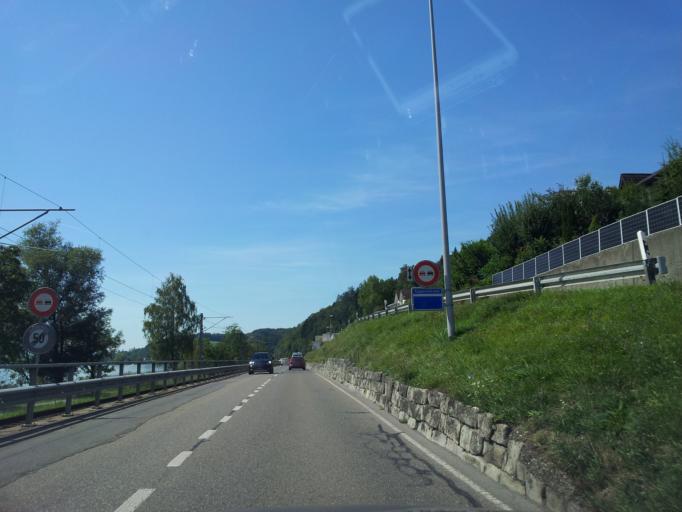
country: CH
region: Saint Gallen
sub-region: Wahlkreis See-Gaster
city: Schmerikon
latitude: 47.2258
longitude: 8.9343
